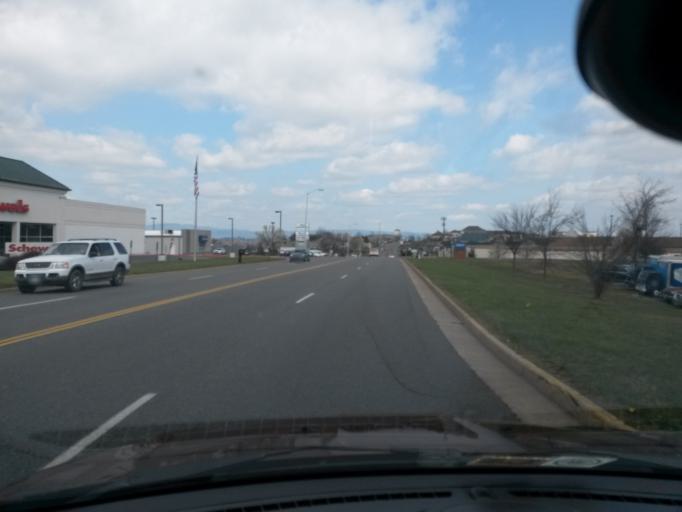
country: US
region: Virginia
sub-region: Rockingham County
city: Massanetta Springs
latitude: 38.4250
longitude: -78.8460
